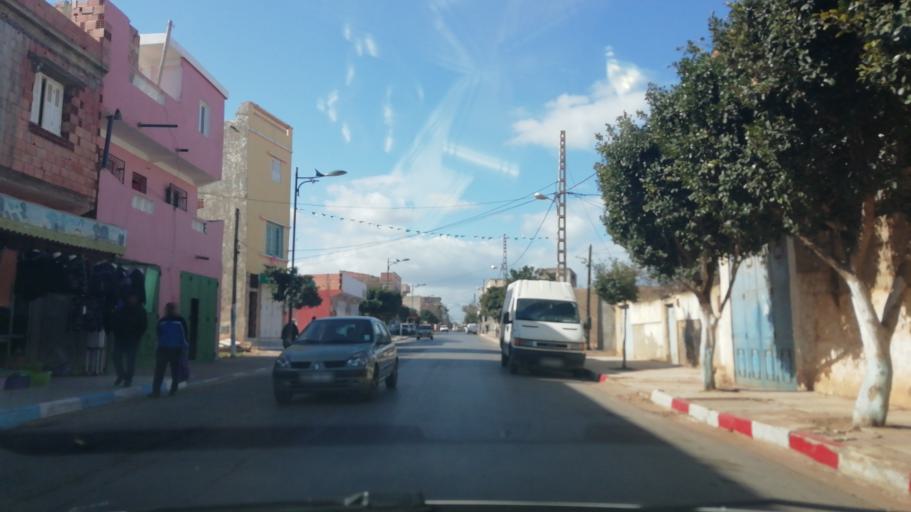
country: DZ
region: Relizane
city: Mazouna
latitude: 36.3179
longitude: 0.6674
